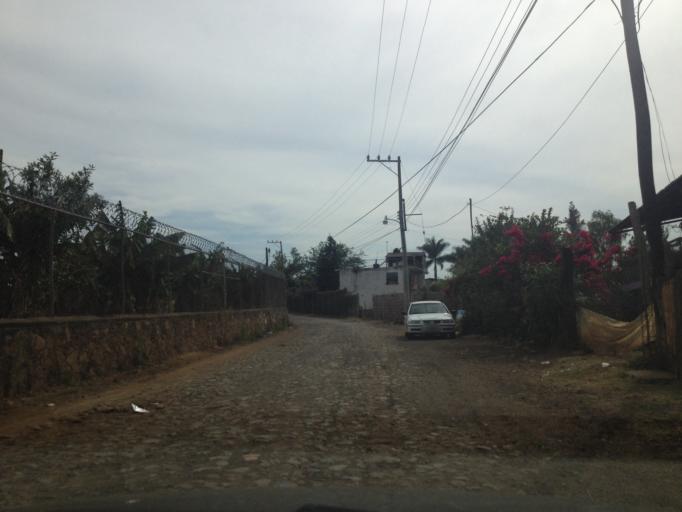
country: MX
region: Michoacan
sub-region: Ziracuaretiro
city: Patuan
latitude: 19.4334
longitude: -101.9255
